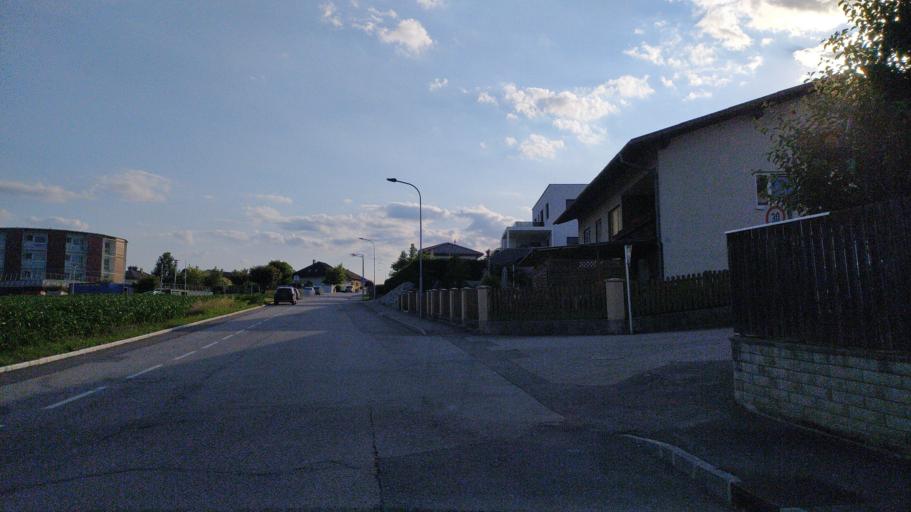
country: AT
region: Lower Austria
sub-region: Politischer Bezirk Amstetten
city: Strengberg
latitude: 48.1636
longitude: 14.7194
